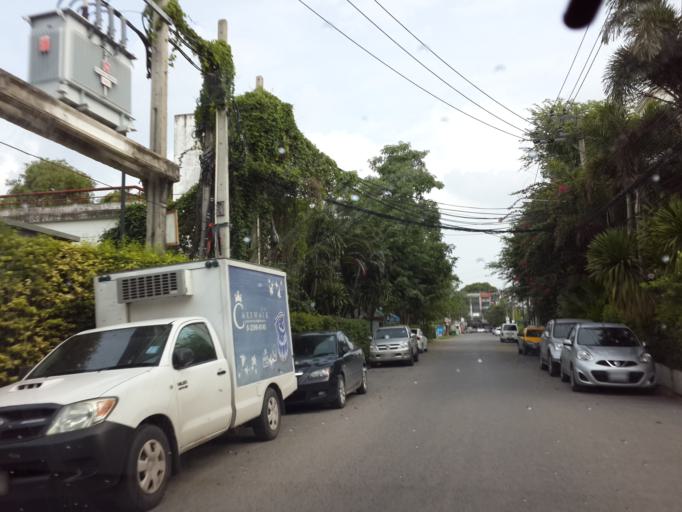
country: TH
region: Bangkok
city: Huai Khwang
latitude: 13.7715
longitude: 100.5906
